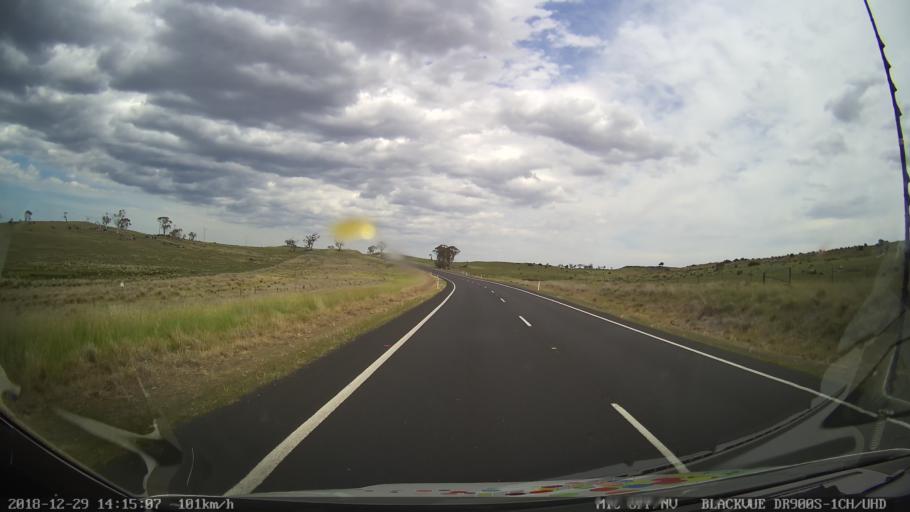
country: AU
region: New South Wales
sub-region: Cooma-Monaro
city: Cooma
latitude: -36.4516
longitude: 149.2380
